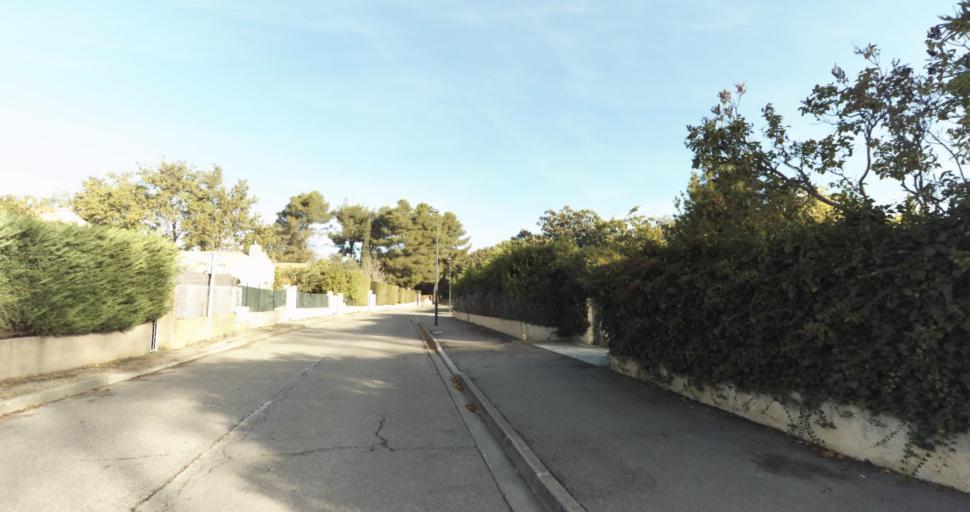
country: FR
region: Provence-Alpes-Cote d'Azur
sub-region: Departement des Bouches-du-Rhone
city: Venelles
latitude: 43.5899
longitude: 5.4679
